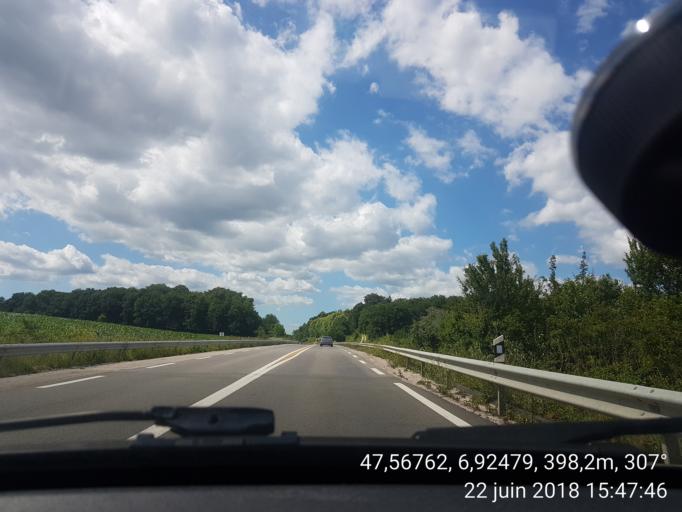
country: FR
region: Franche-Comte
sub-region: Territoire de Belfort
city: Bourogne
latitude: 47.5674
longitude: 6.9252
